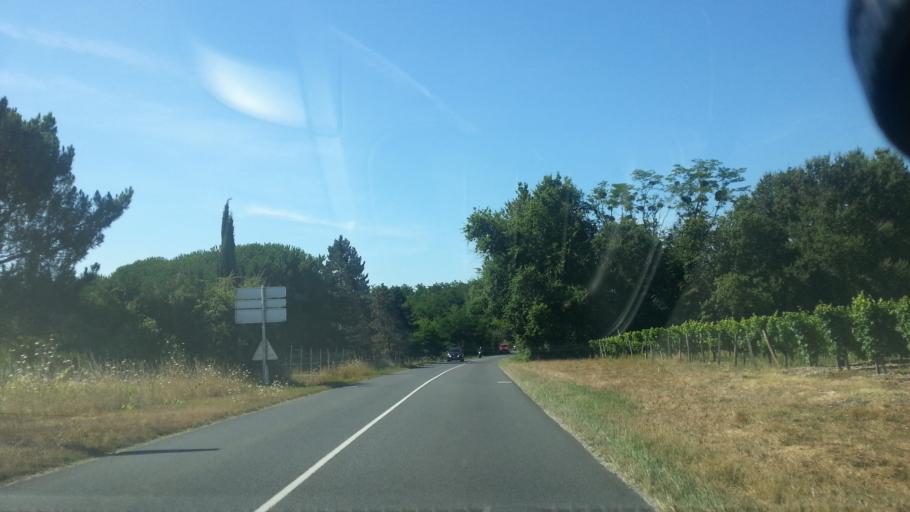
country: FR
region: Aquitaine
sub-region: Departement de la Gironde
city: Illats
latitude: 44.6250
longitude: -0.3696
